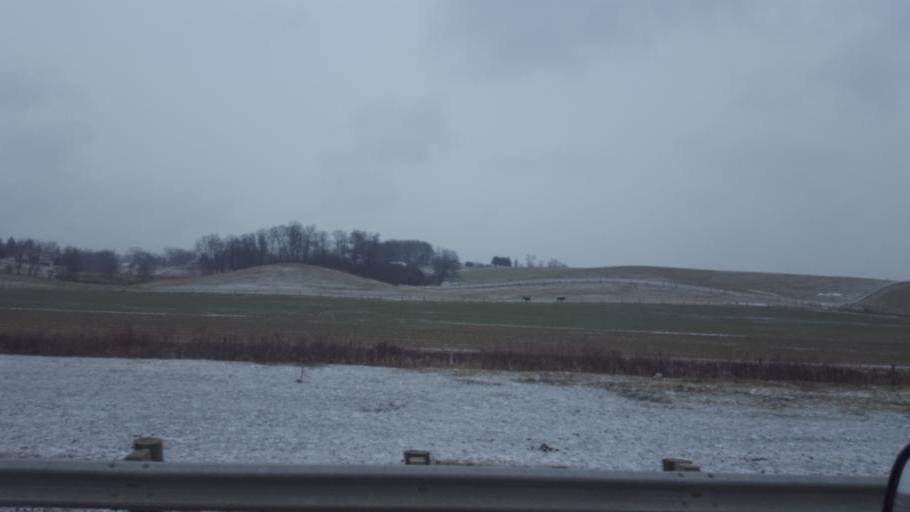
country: US
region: Ohio
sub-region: Tuscarawas County
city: Sugarcreek
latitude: 40.4794
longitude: -81.7338
